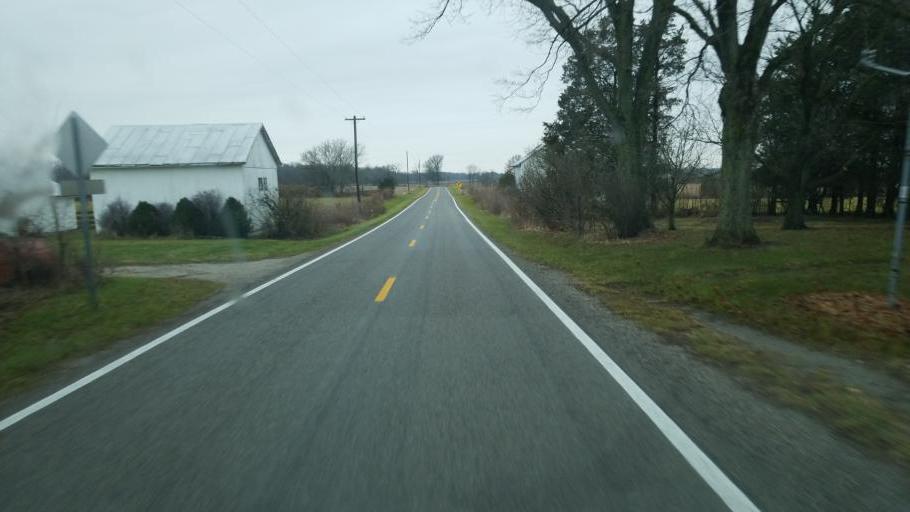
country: US
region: Ohio
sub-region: Delaware County
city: Ashley
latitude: 40.3575
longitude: -82.9976
